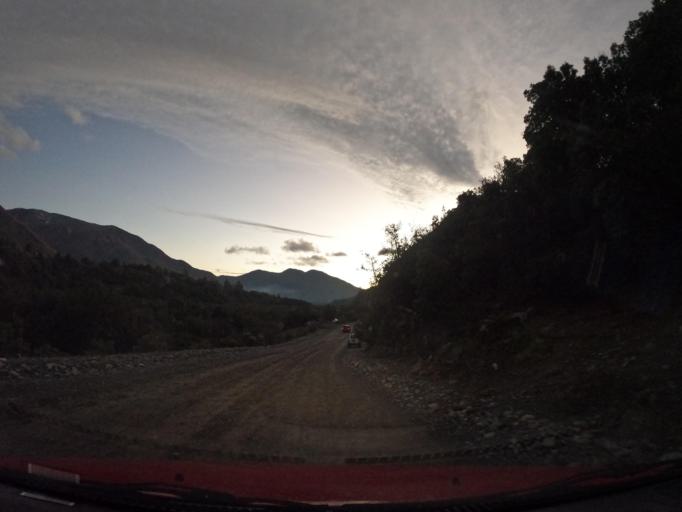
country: CL
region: Maule
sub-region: Provincia de Linares
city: Colbun
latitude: -35.8582
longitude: -71.2092
